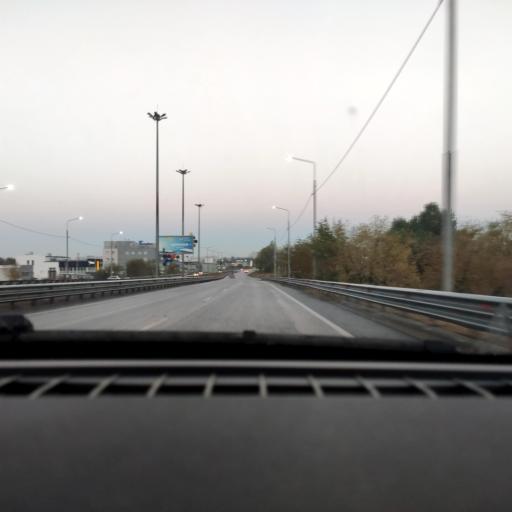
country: RU
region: Voronezj
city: Somovo
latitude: 51.6779
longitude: 39.2981
